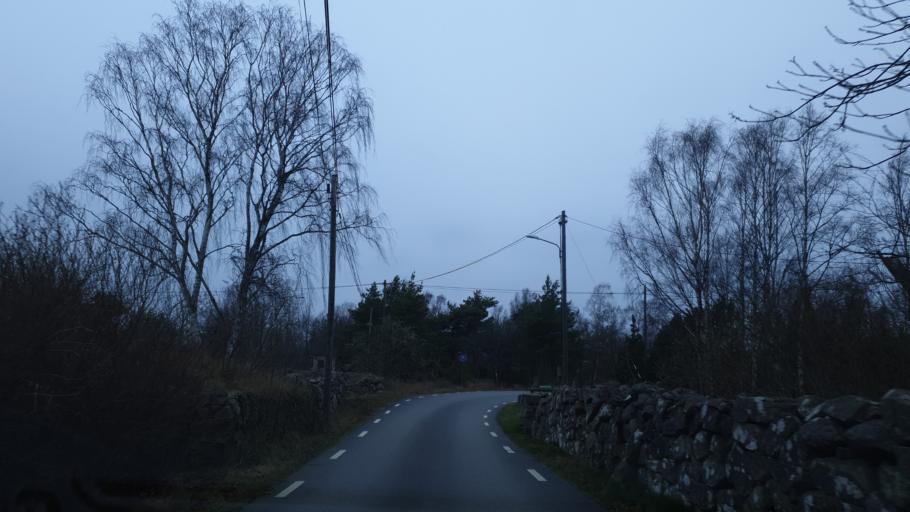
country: SE
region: Blekinge
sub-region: Karlskrona Kommun
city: Karlskrona
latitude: 56.1087
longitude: 15.6114
